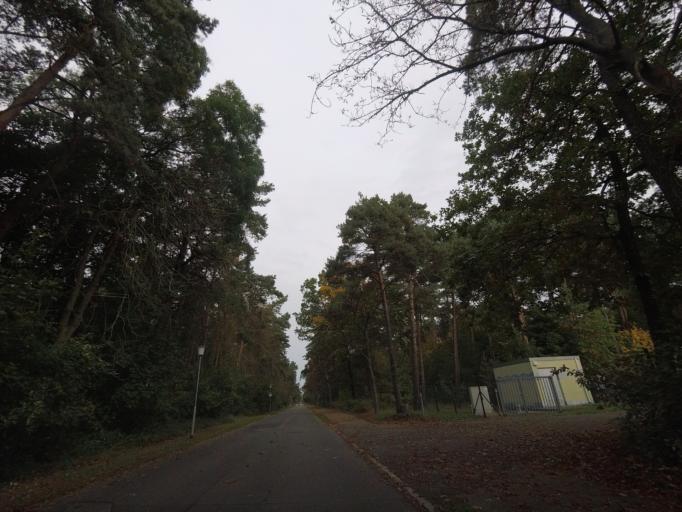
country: DE
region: Brandenburg
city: Niedergorsdorf
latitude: 52.0056
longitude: 12.9942
